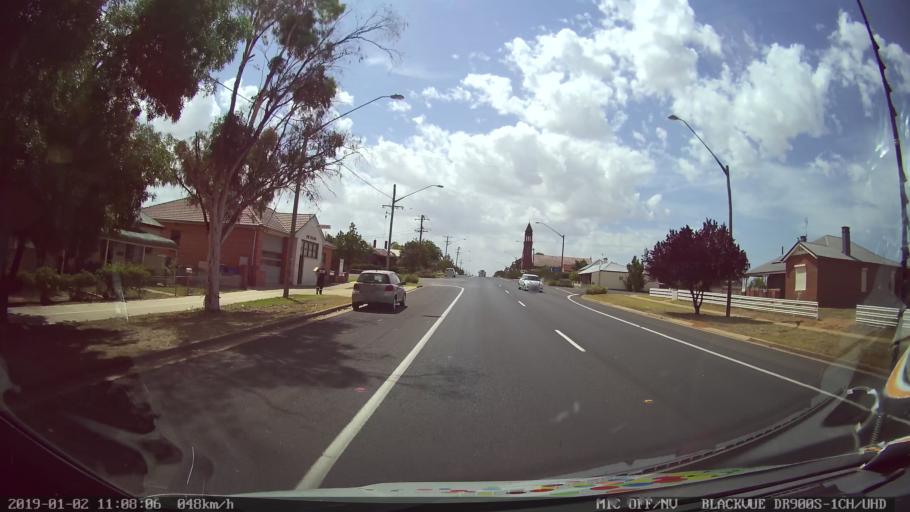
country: AU
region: New South Wales
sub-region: Young
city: Young
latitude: -34.5531
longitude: 148.3644
